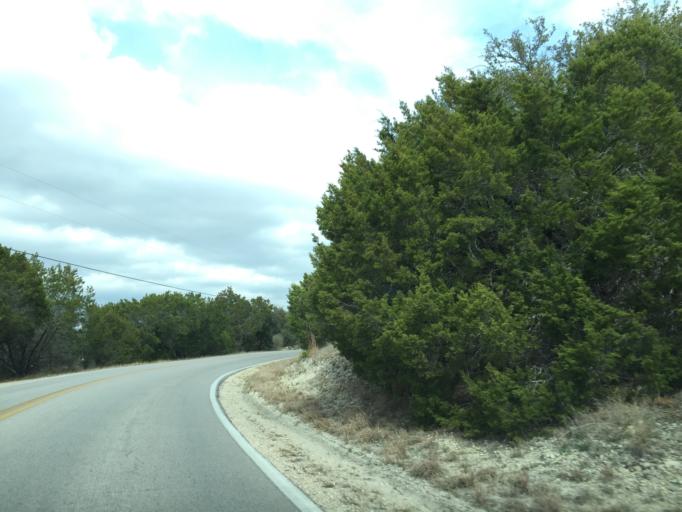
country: US
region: Texas
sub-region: Travis County
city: Briarcliff
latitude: 30.3742
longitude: -98.0866
